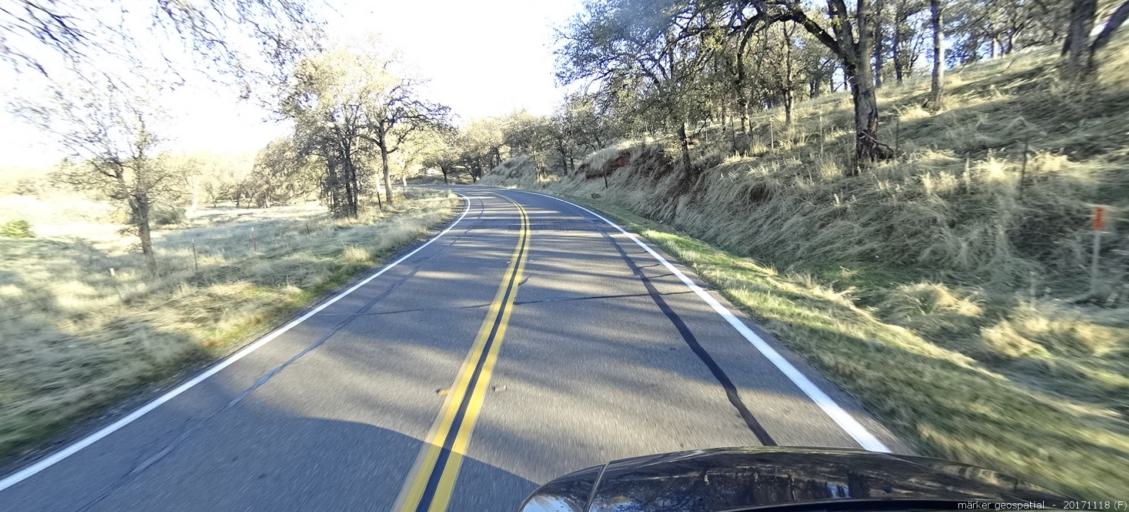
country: US
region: California
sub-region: Shasta County
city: Cottonwood
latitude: 40.4121
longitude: -122.2825
